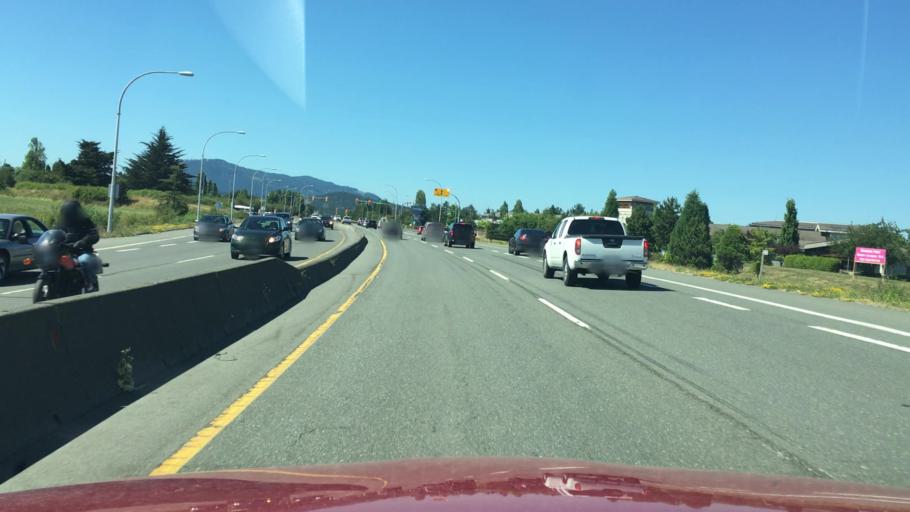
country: CA
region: British Columbia
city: North Saanich
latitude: 48.6468
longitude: -123.4056
